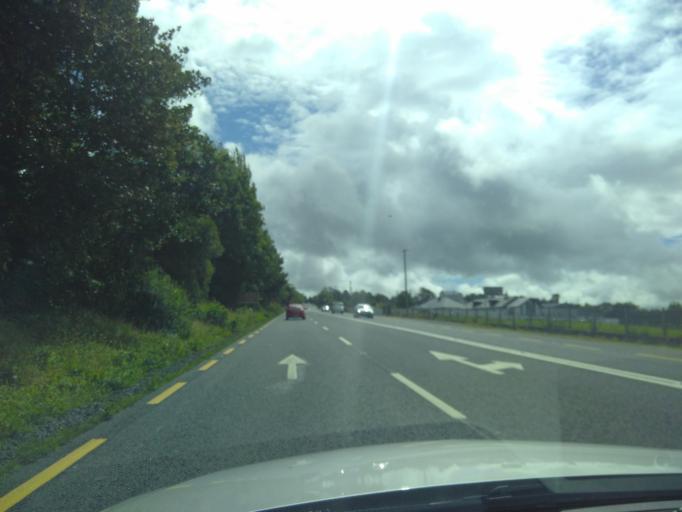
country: IE
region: Ulster
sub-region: County Donegal
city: Letterkenny
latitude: 54.9401
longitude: -7.6959
